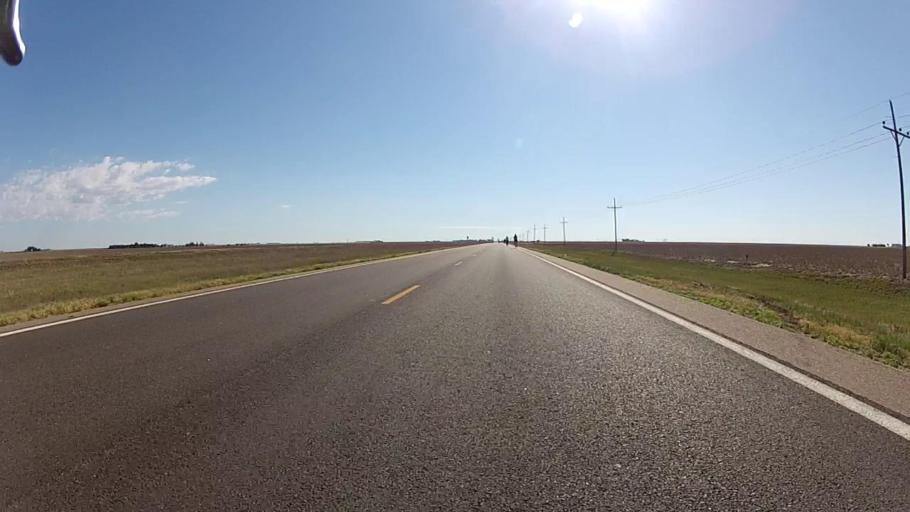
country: US
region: Kansas
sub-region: Gray County
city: Cimarron
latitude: 37.5802
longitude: -100.5106
